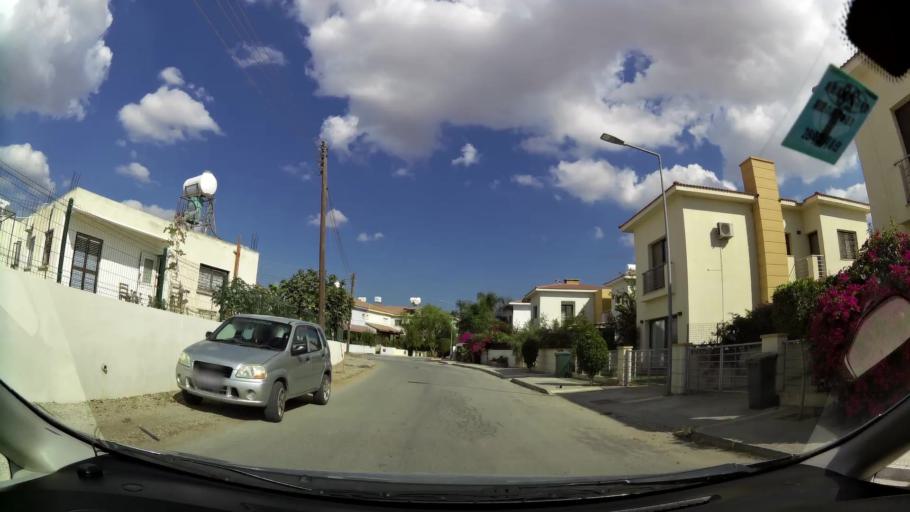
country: CY
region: Lefkosia
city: Nicosia
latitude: 35.2170
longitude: 33.3814
